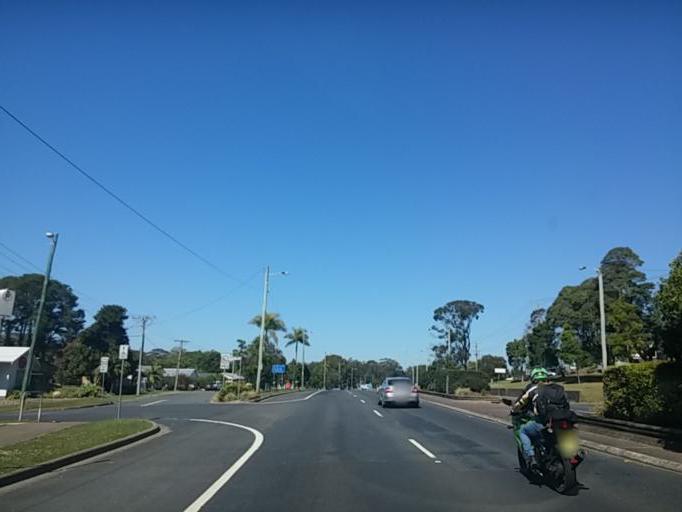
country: AU
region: New South Wales
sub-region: Coffs Harbour
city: Coffs Harbour
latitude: -30.2872
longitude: 153.1242
